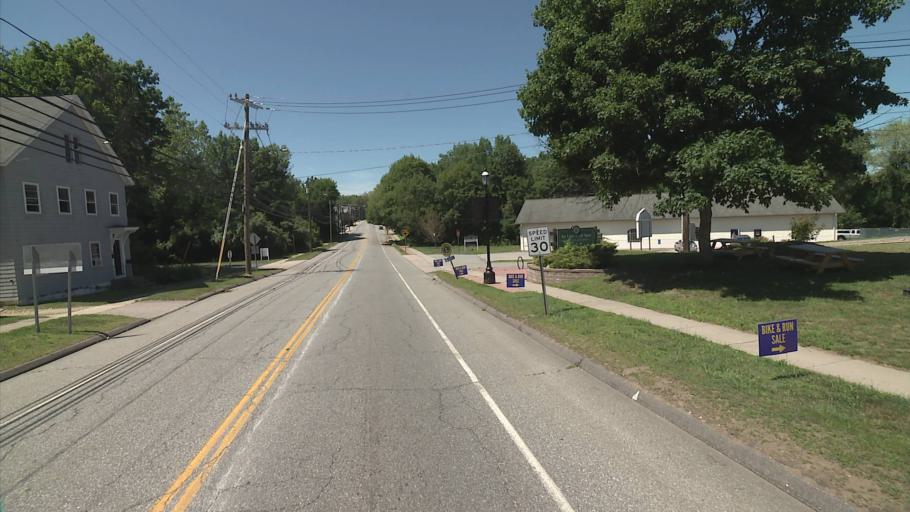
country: US
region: Connecticut
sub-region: New London County
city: Colchester
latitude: 41.5797
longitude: -72.3269
